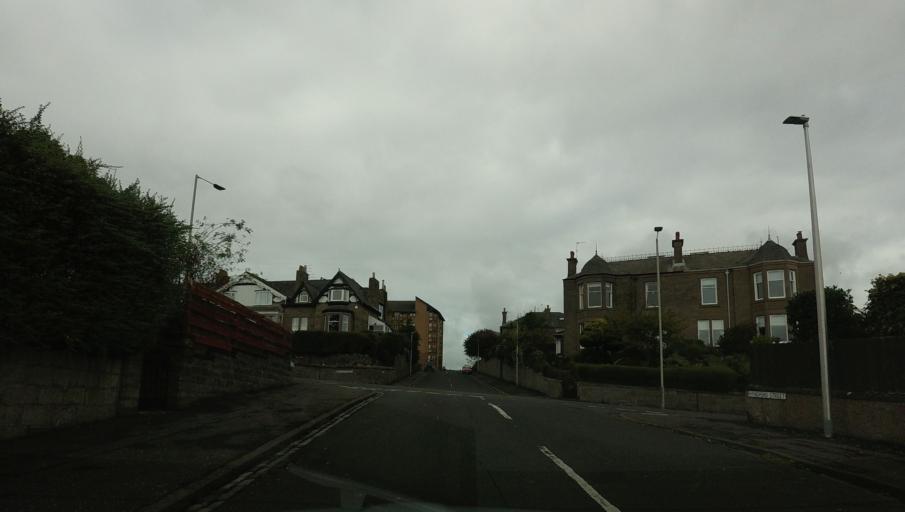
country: GB
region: Scotland
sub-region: Dundee City
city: Dundee
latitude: 56.4596
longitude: -3.0018
